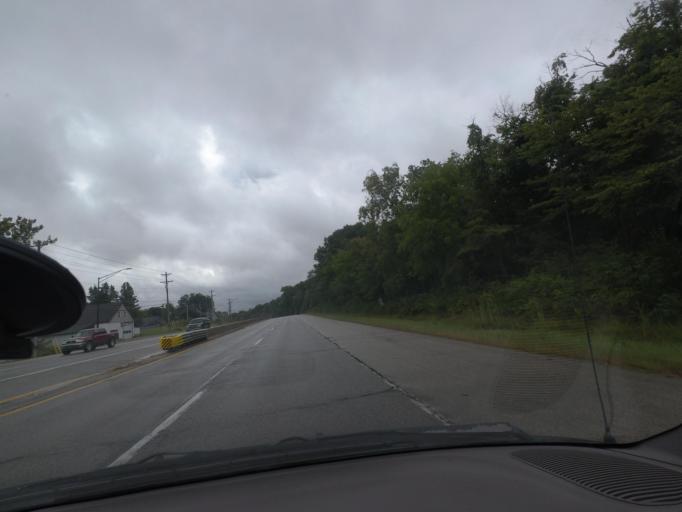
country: US
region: Indiana
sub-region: Montgomery County
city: Crawfordsville
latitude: 40.0613
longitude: -86.9087
